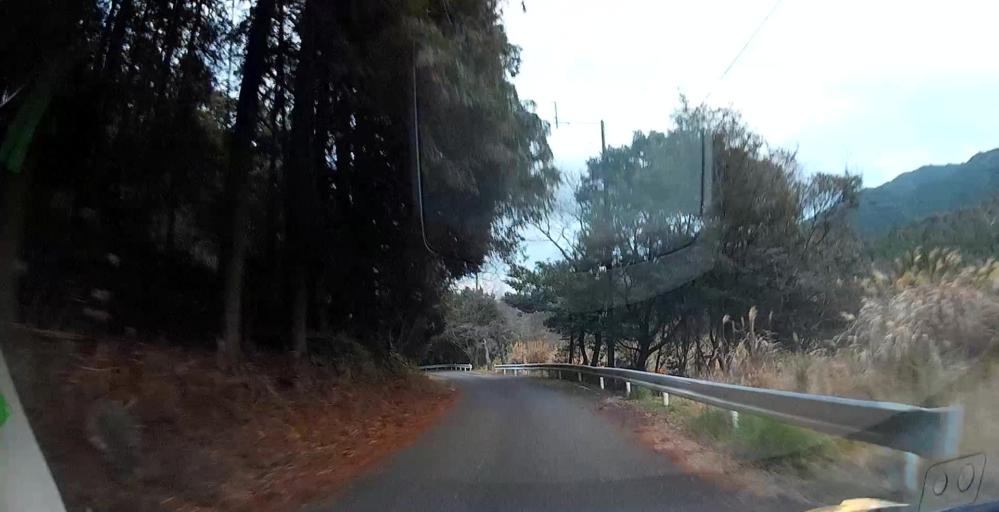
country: JP
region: Kagoshima
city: Izumi
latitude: 32.1204
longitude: 130.4153
